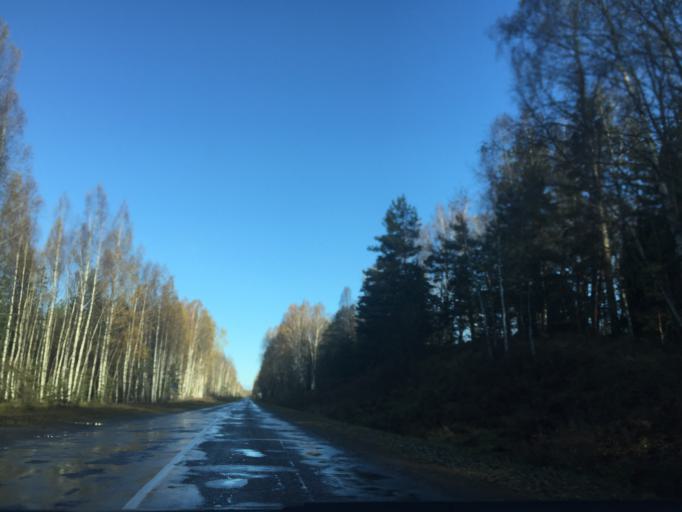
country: LV
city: Tireli
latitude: 56.8991
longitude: 23.5309
